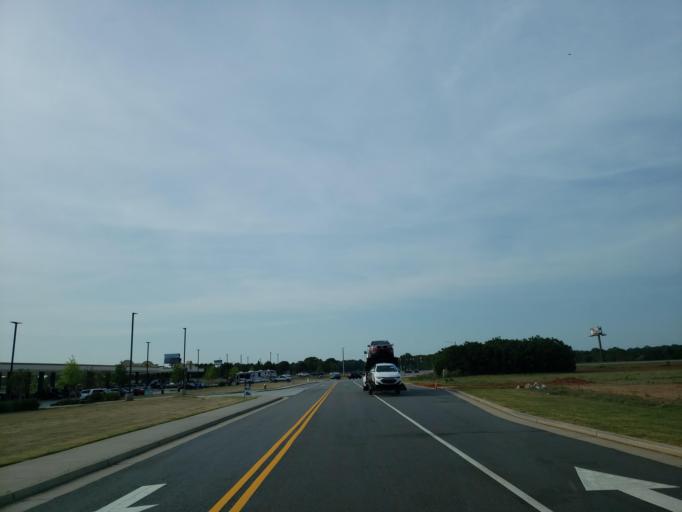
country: US
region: Georgia
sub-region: Houston County
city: Centerville
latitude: 32.5837
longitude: -83.7391
